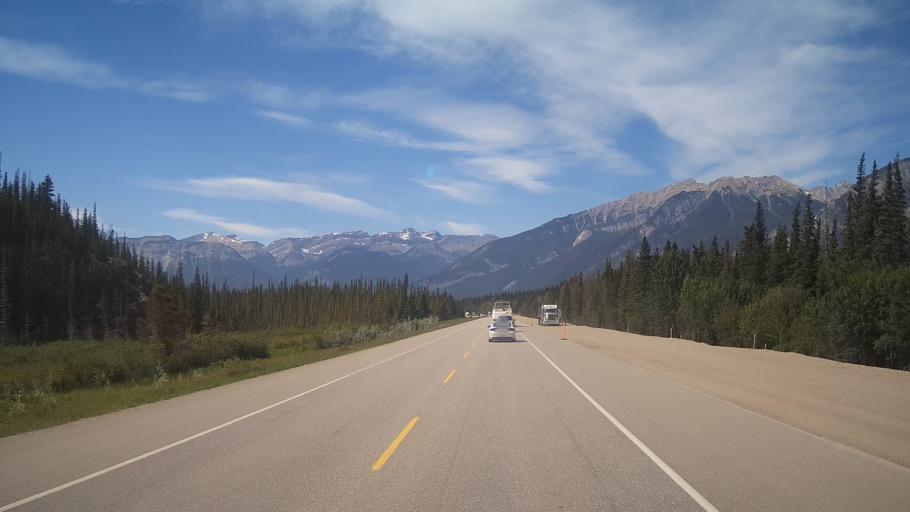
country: CA
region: Alberta
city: Jasper Park Lodge
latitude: 53.0730
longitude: -118.0484
